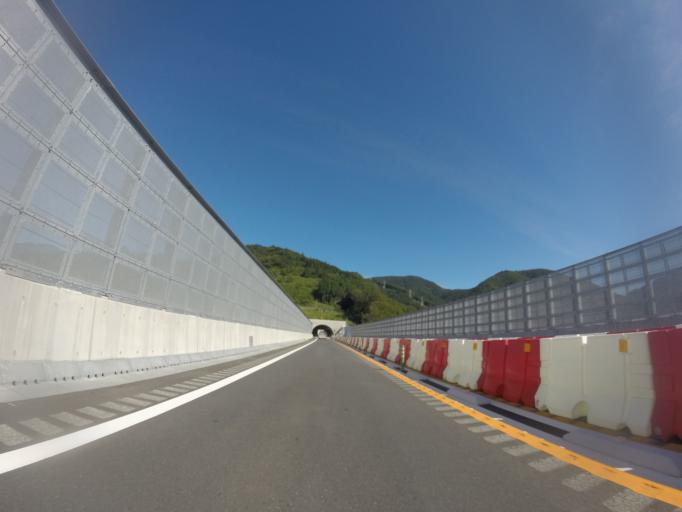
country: JP
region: Yamanashi
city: Ryuo
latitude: 35.4194
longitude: 138.4621
